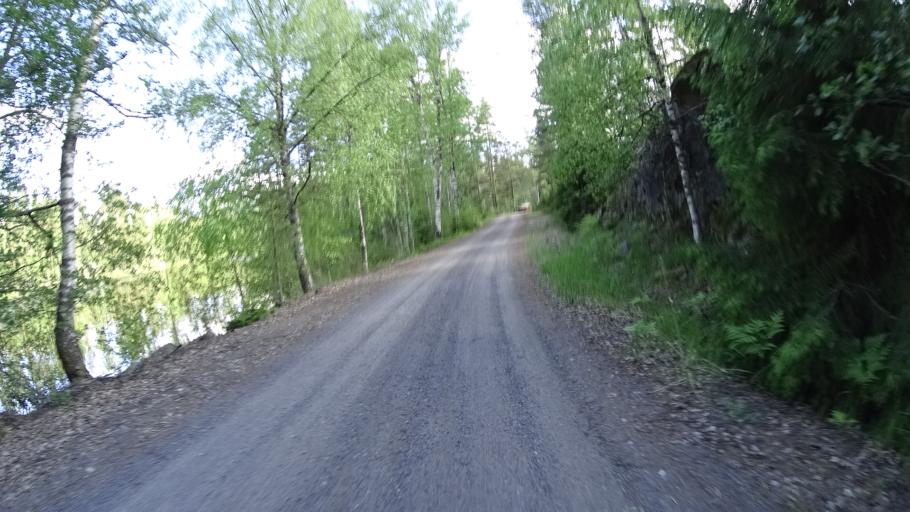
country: FI
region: Varsinais-Suomi
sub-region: Salo
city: Kisko
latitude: 60.1658
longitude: 23.4914
